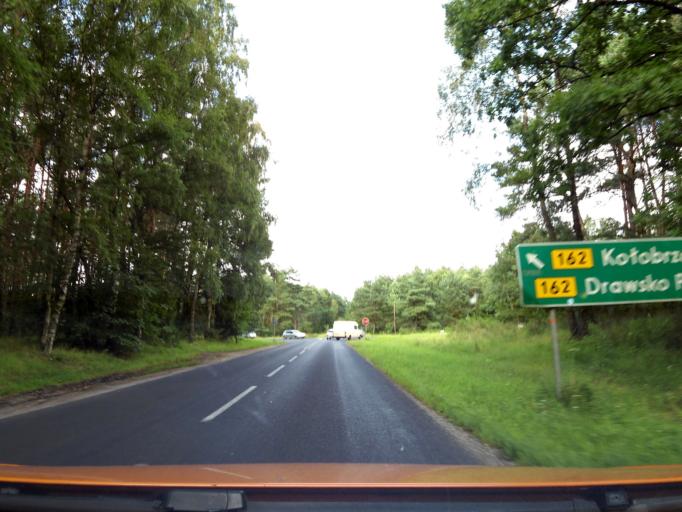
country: PL
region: West Pomeranian Voivodeship
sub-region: Powiat kolobrzeski
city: Kolobrzeg
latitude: 54.1170
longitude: 15.5879
